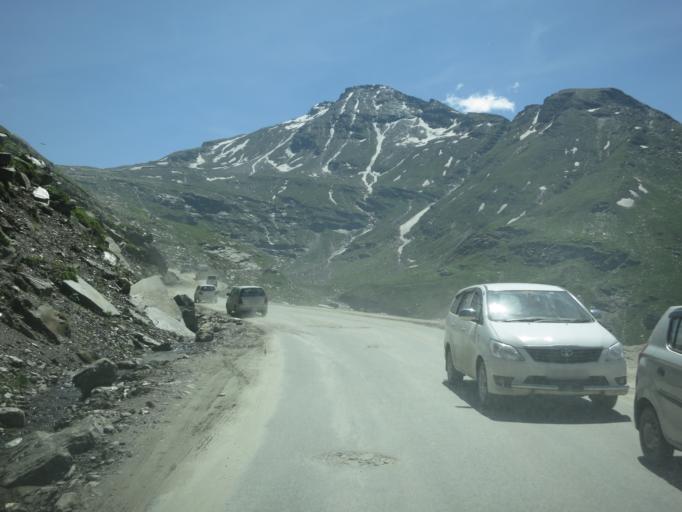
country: IN
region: Himachal Pradesh
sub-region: Kulu
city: Manali
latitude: 32.3550
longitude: 77.2237
